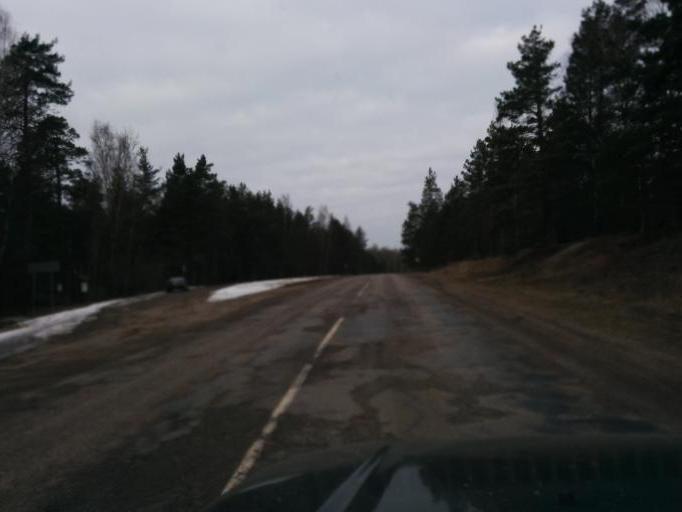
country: LV
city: Tireli
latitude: 56.8946
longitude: 23.5348
